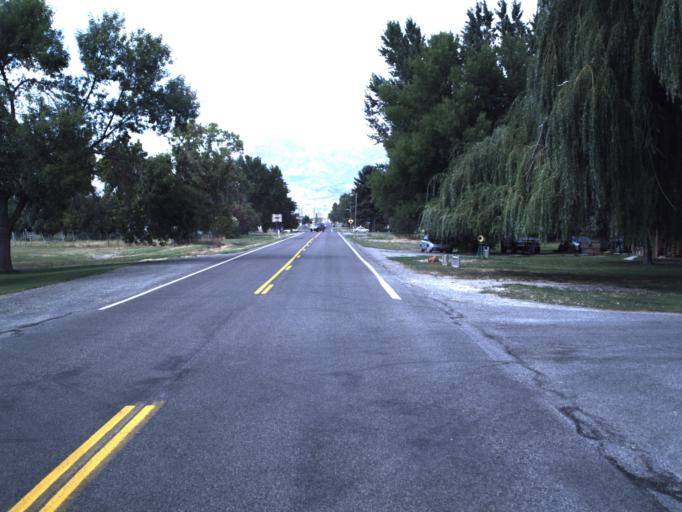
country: US
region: Utah
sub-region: Box Elder County
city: Garland
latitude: 41.8111
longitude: -112.1160
